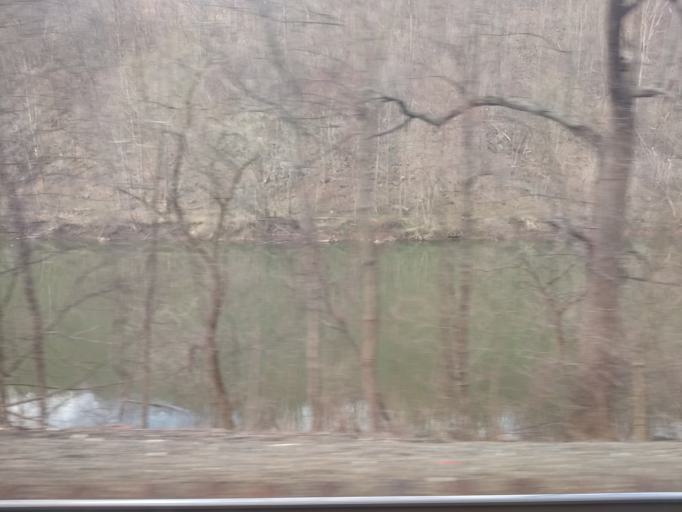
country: US
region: Pennsylvania
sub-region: Huntingdon County
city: Huntingdon
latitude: 40.5222
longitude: -78.0256
